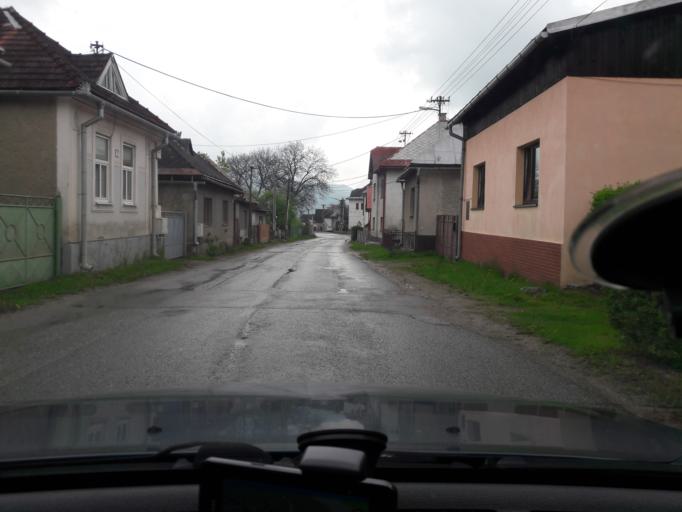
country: SK
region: Banskobystricky
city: Revuca
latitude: 48.7401
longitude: 20.0444
